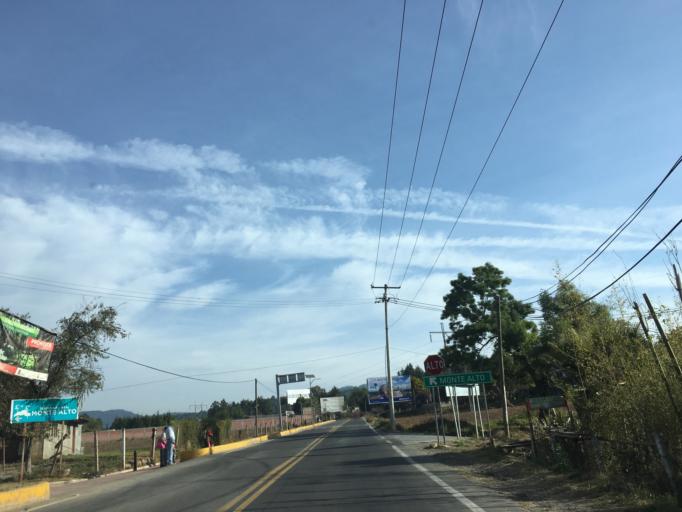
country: MX
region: Mexico
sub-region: Valle de Bravo
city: Colonia Rincon Villa del Valle
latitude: 19.1909
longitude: -100.1009
